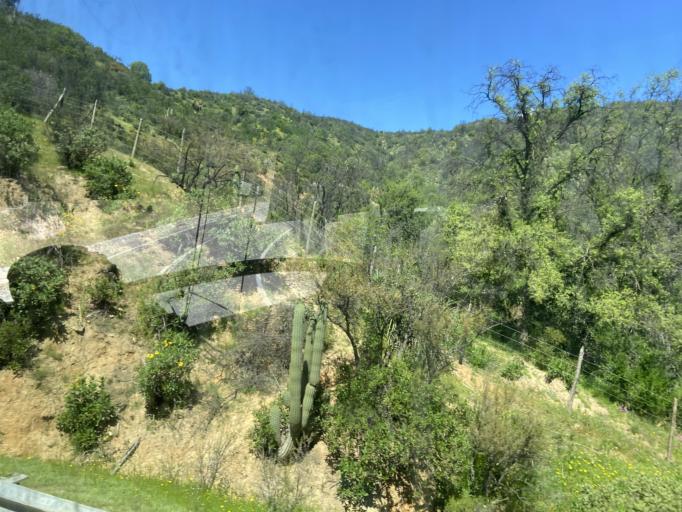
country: CL
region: Valparaiso
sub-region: Provincia de Marga Marga
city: Villa Alemana
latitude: -33.1905
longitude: -71.2893
